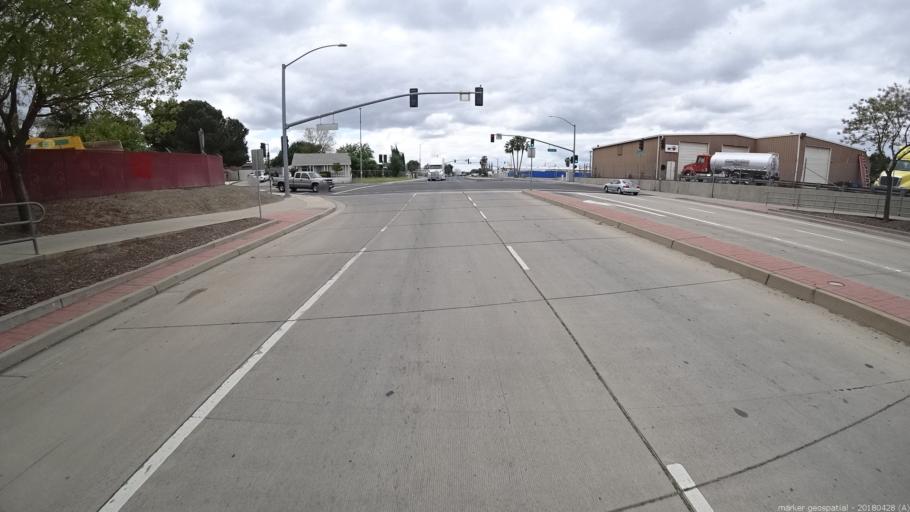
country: US
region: California
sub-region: Yolo County
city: West Sacramento
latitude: 38.5865
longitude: -121.5466
